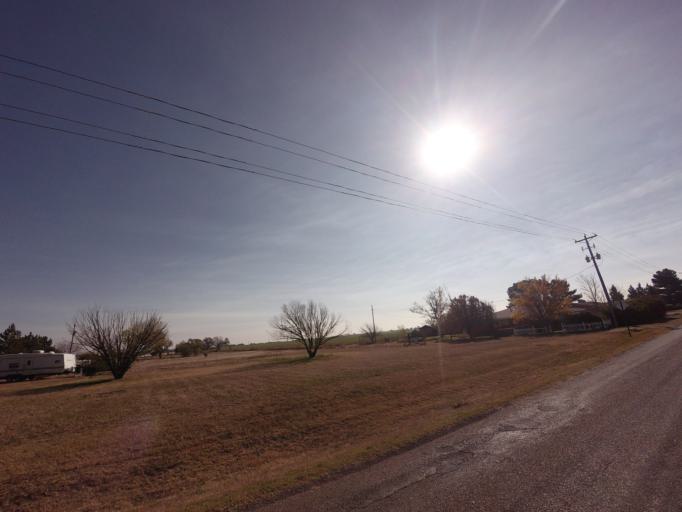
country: US
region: New Mexico
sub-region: Curry County
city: Clovis
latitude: 34.4179
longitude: -103.1607
